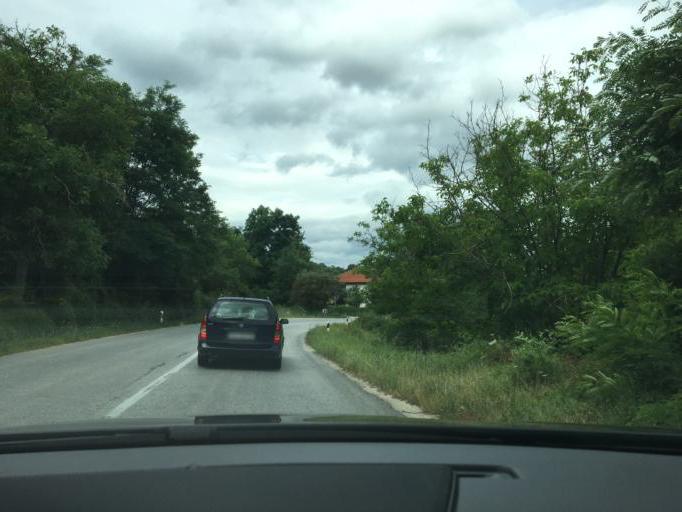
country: MK
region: Opstina Rankovce
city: Rankovce
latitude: 42.1723
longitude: 22.2114
